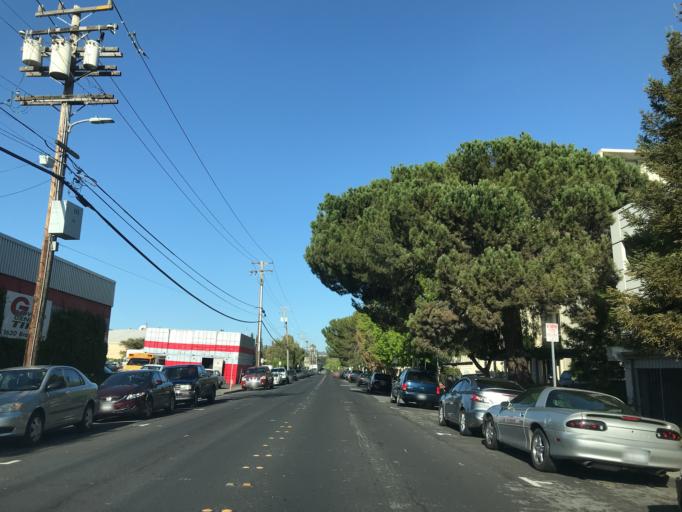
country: US
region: California
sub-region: San Mateo County
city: Redwood City
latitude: 37.4878
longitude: -122.2188
